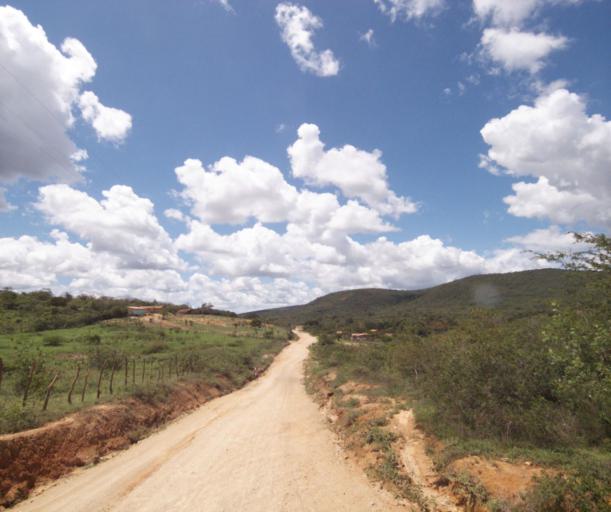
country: BR
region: Bahia
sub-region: Pocoes
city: Pocoes
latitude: -14.3853
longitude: -40.5535
